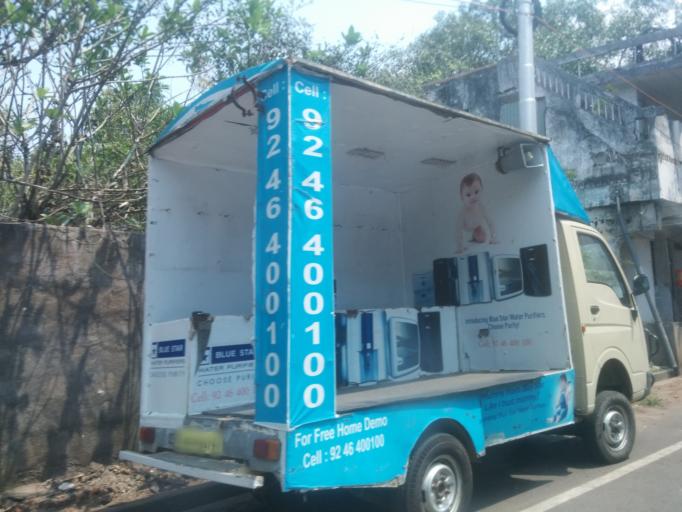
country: IN
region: Andhra Pradesh
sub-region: East Godavari
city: Rajahmundry
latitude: 17.0165
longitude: 81.7805
